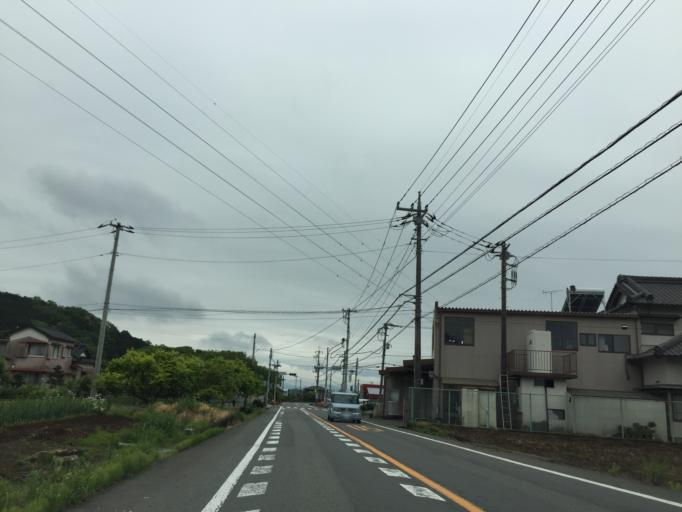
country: JP
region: Shizuoka
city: Mishima
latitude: 35.1887
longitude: 138.9215
